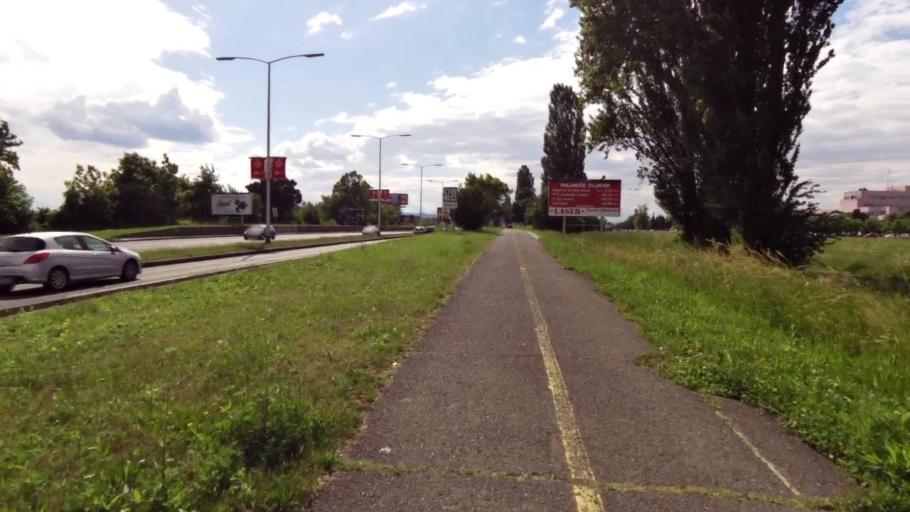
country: HR
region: Grad Zagreb
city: Stenjevec
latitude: 45.7975
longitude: 15.8804
